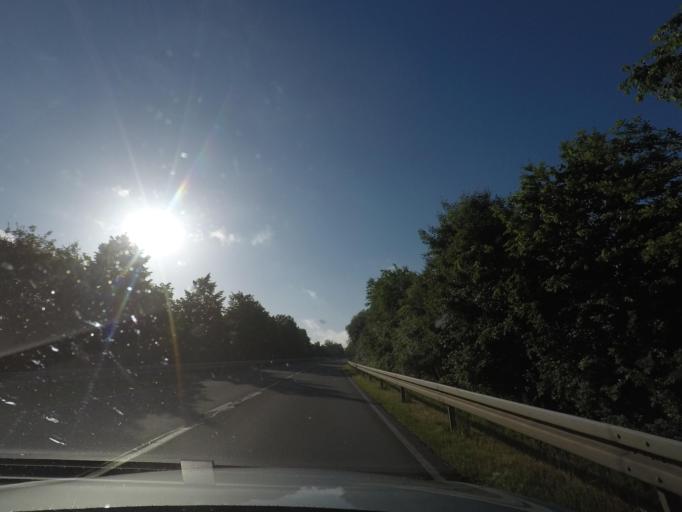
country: DE
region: Saxony-Anhalt
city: Huy-Neinstedt
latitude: 51.9704
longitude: 10.8486
